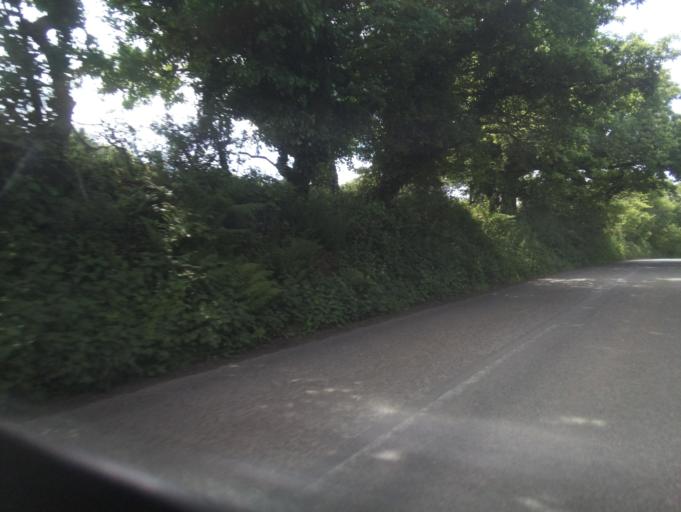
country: GB
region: England
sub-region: Devon
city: Kingsbridge
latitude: 50.3606
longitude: -3.7525
